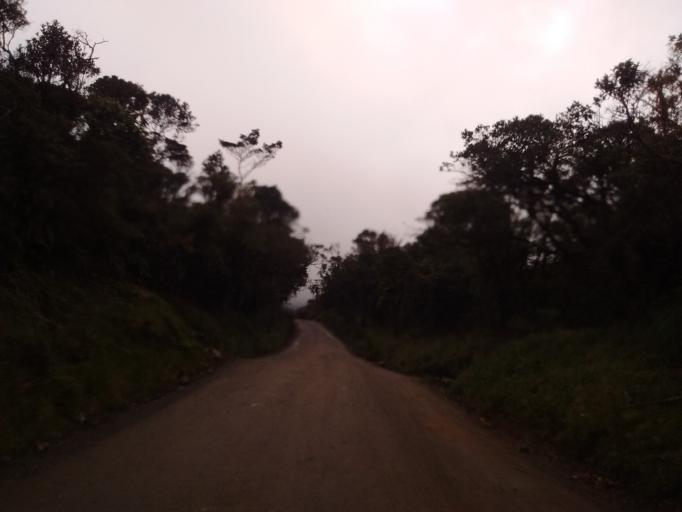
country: CO
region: Huila
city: Isnos
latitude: 2.1208
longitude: -76.3765
